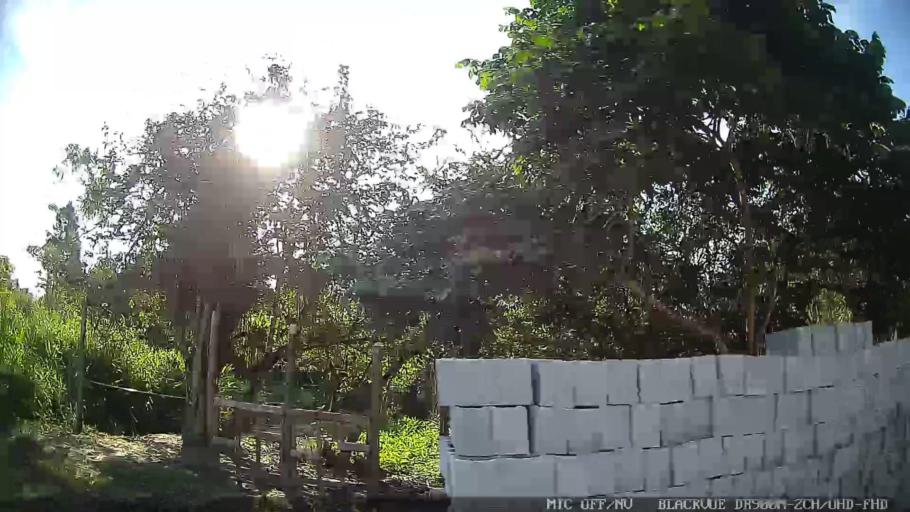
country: BR
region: Sao Paulo
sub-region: Itanhaem
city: Itanhaem
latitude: -24.1746
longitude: -46.8220
